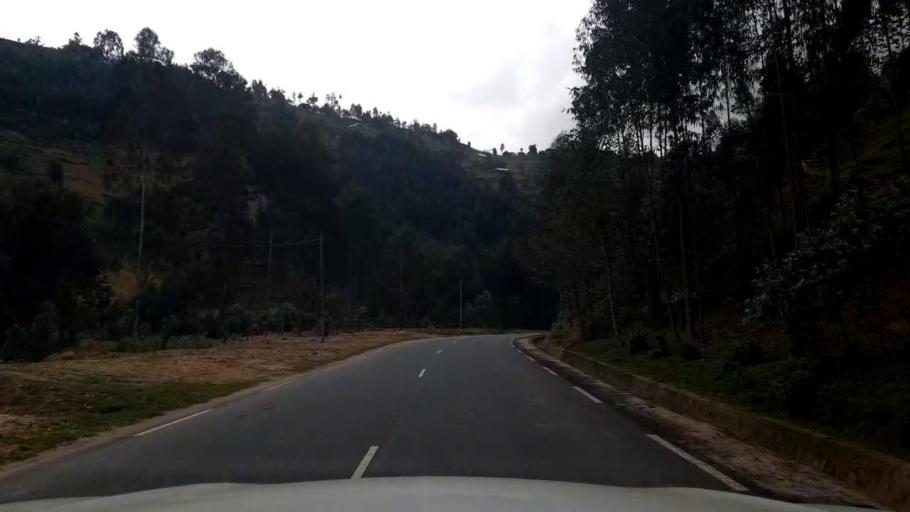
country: RW
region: Northern Province
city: Musanze
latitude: -1.6952
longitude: 29.5566
